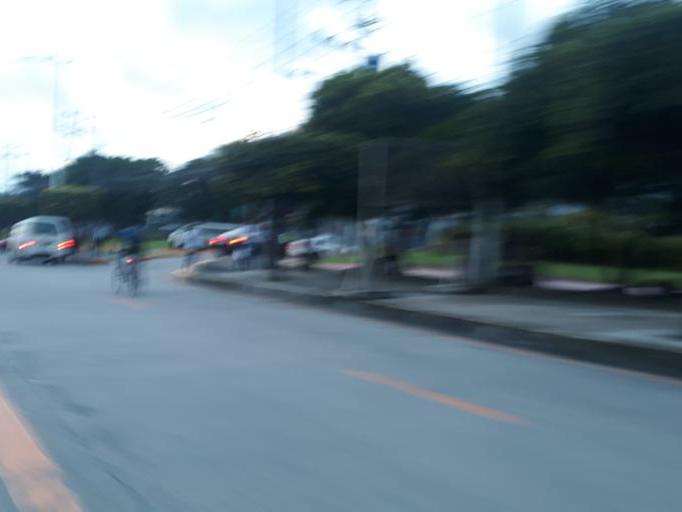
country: PH
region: Metro Manila
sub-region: Quezon City
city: Quezon City
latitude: 14.6592
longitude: 121.0608
